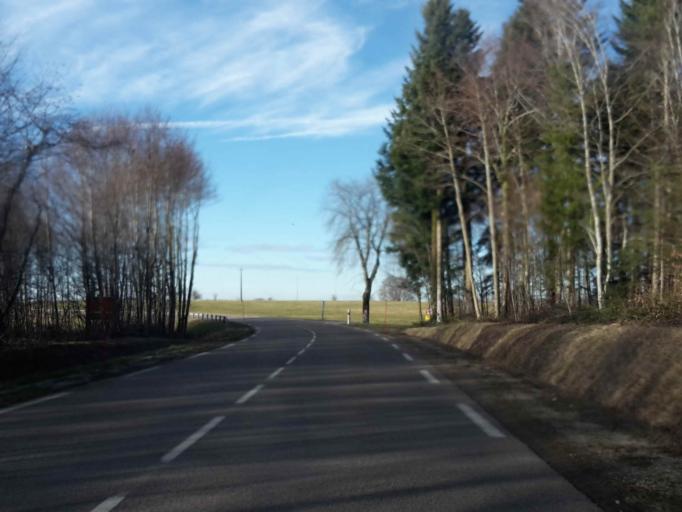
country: FR
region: Franche-Comte
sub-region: Departement du Doubs
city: Vercel-Villedieu-le-Camp
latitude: 47.2031
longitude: 6.3951
